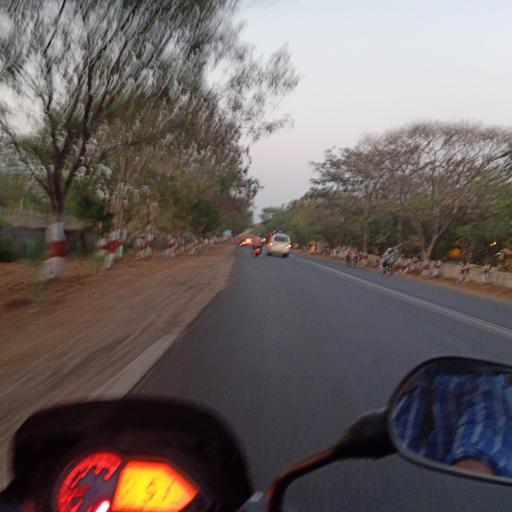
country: IN
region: Telangana
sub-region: Rangareddi
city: Secunderabad
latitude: 17.5443
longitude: 78.5337
